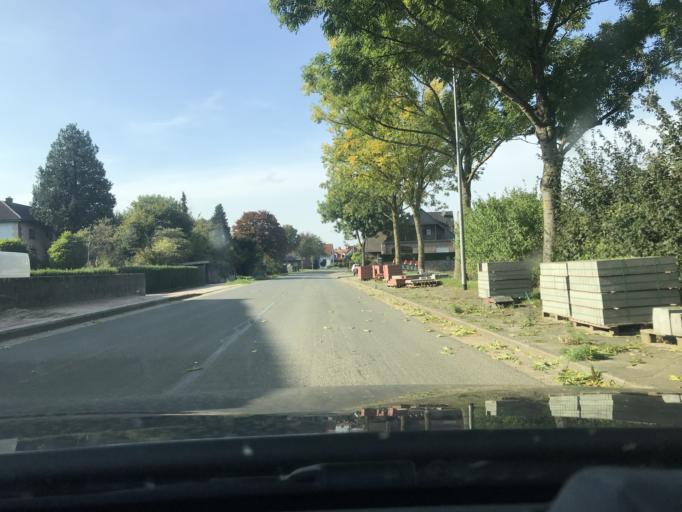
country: DE
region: North Rhine-Westphalia
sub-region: Regierungsbezirk Dusseldorf
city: Emmerich
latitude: 51.8041
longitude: 6.2085
